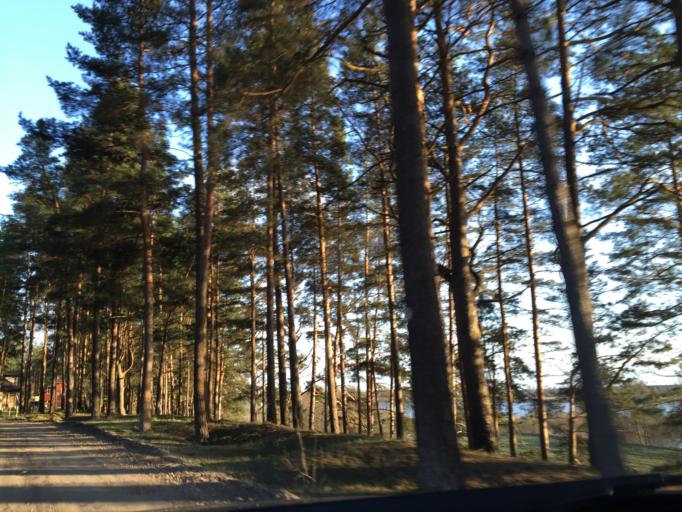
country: LV
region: Kekava
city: Kekava
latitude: 56.8567
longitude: 24.2218
